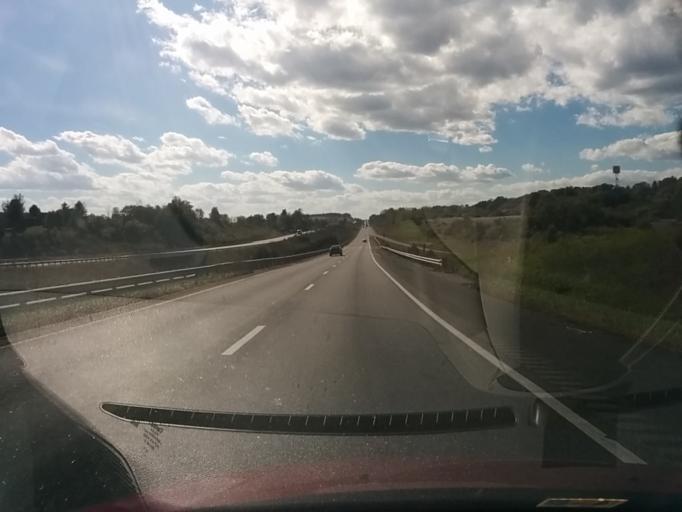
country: US
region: Virginia
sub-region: City of Buena Vista
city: Buena Vista
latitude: 37.8867
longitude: -79.2838
